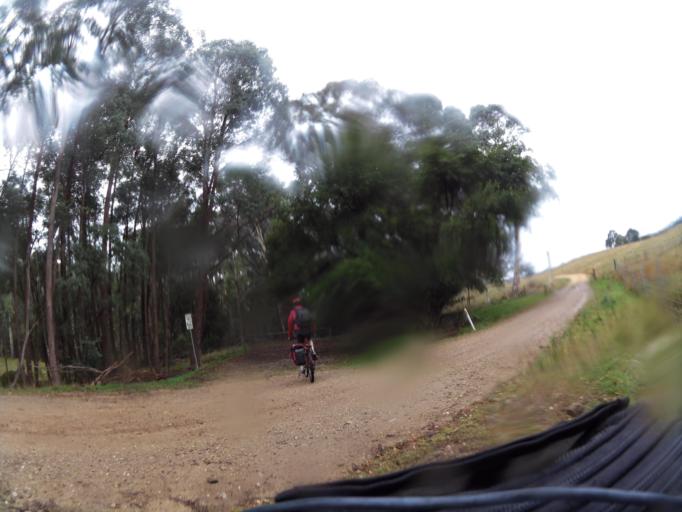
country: AU
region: New South Wales
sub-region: Greater Hume Shire
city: Holbrook
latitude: -36.1619
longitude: 147.4866
